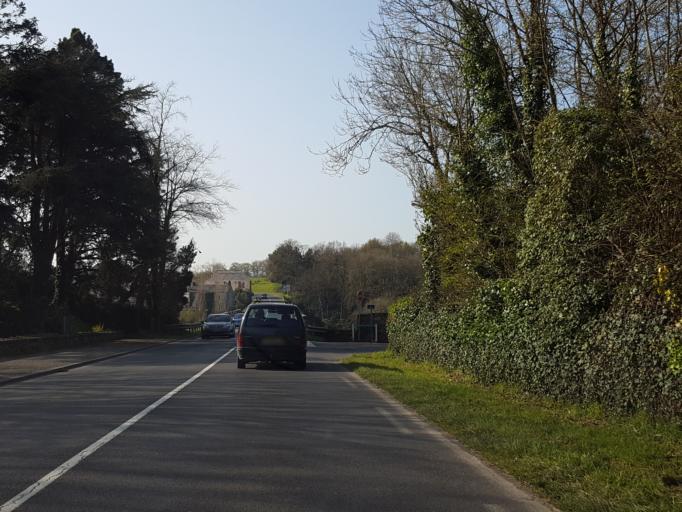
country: FR
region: Pays de la Loire
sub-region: Departement de la Vendee
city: Rocheserviere
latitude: 46.9368
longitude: -1.5143
